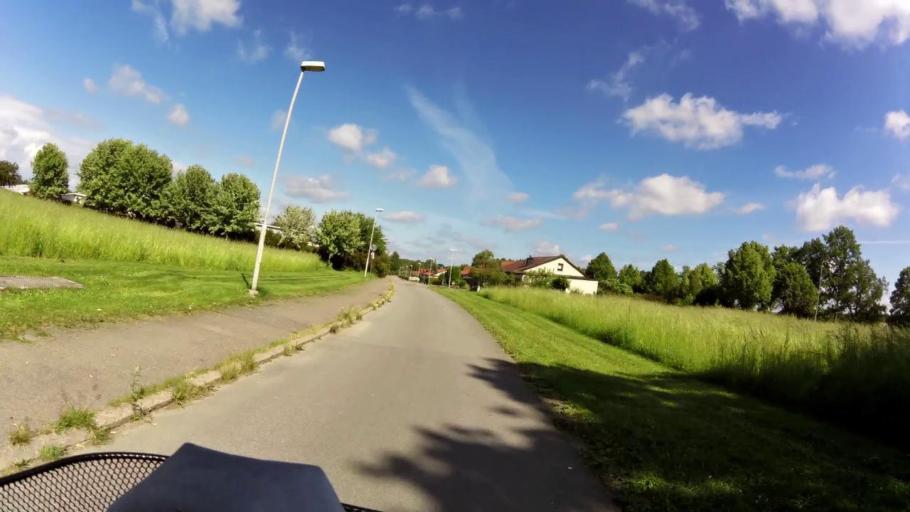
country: SE
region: OEstergoetland
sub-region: Linkopings Kommun
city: Linkoping
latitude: 58.3829
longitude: 15.6408
